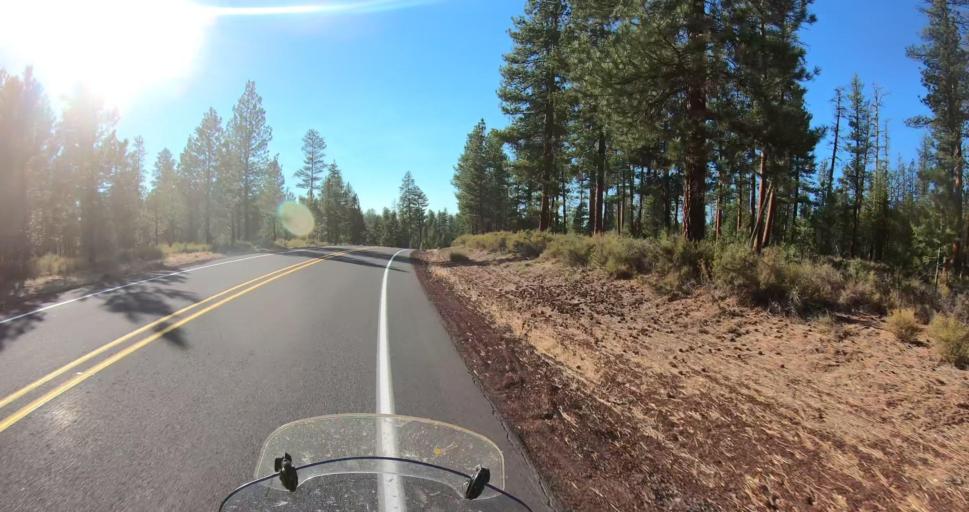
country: US
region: Oregon
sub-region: Deschutes County
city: La Pine
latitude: 43.4678
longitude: -121.3936
